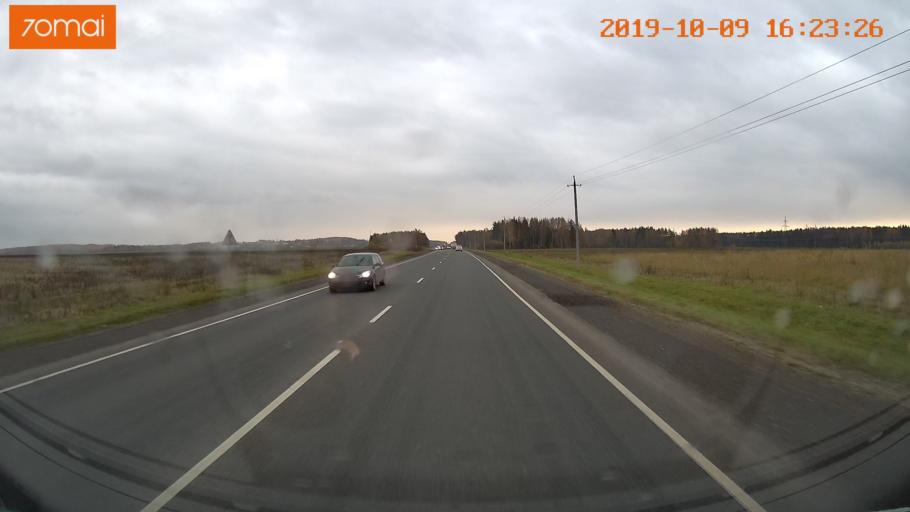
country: RU
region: Kostroma
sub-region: Kostromskoy Rayon
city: Kostroma
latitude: 57.6642
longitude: 40.8989
